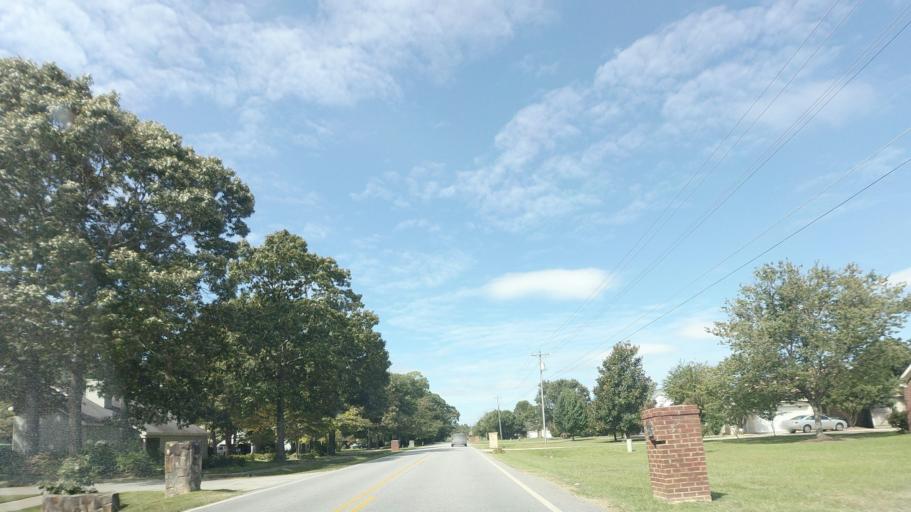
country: US
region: Georgia
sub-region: Houston County
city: Centerville
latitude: 32.6103
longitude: -83.6920
